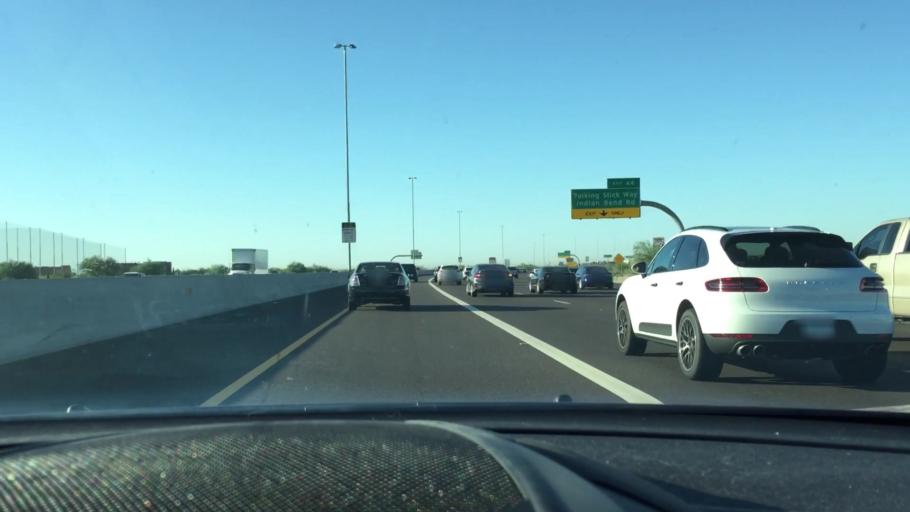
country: US
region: Arizona
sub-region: Maricopa County
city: Scottsdale
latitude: 33.5483
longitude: -111.8799
